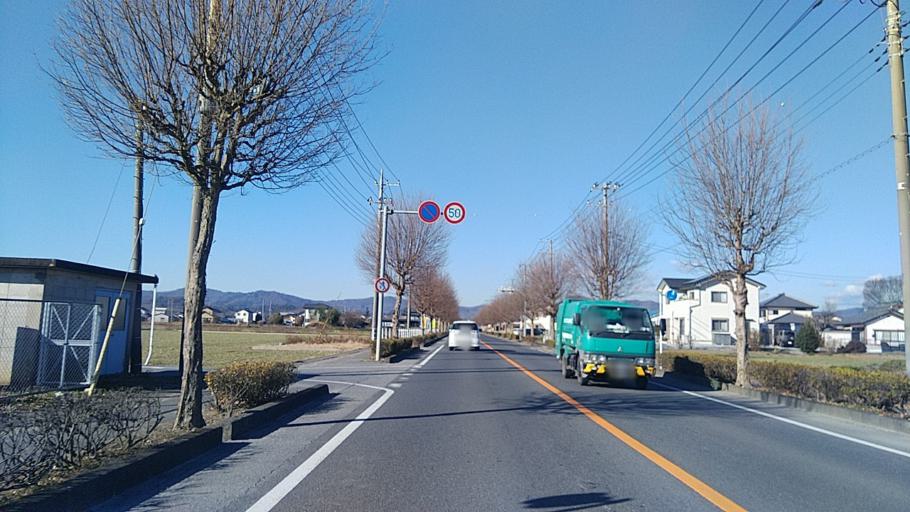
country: JP
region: Tochigi
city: Tanuma
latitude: 36.3454
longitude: 139.5651
